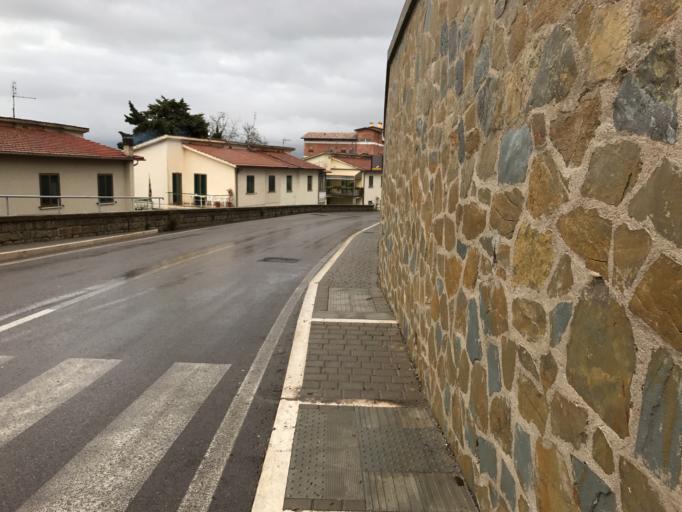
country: IT
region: Umbria
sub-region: Provincia di Perugia
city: Perugia
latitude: 43.1143
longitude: 12.4026
